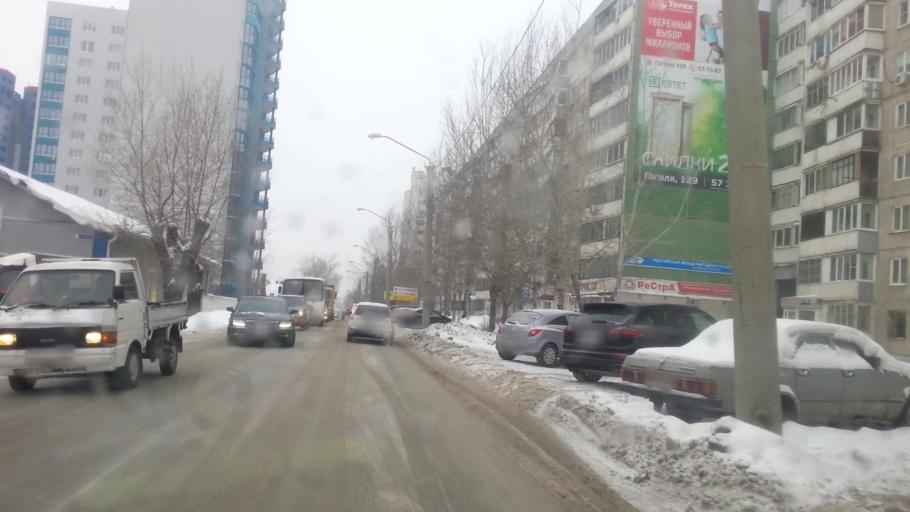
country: RU
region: Altai Krai
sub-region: Gorod Barnaulskiy
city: Barnaul
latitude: 53.3356
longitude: 83.7746
